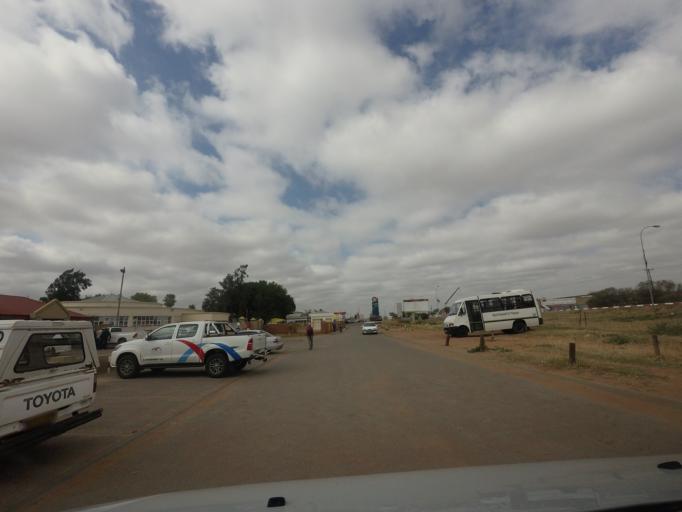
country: BW
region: Central
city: Palapye
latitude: -22.5387
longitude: 27.0892
